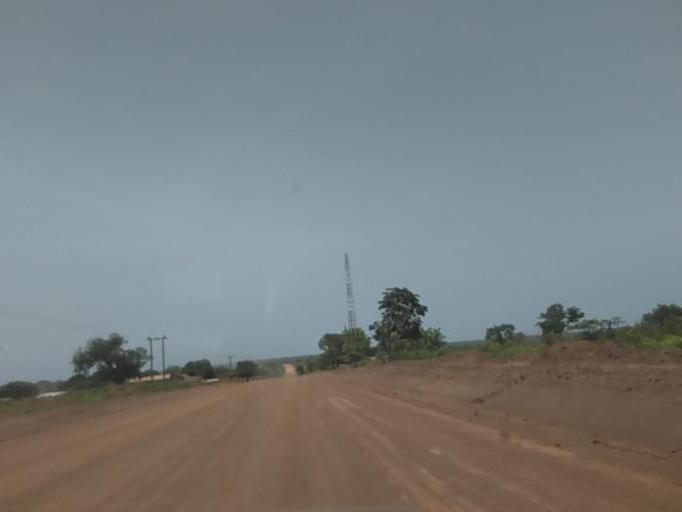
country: GH
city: Kpandae
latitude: 8.6344
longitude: 0.2234
